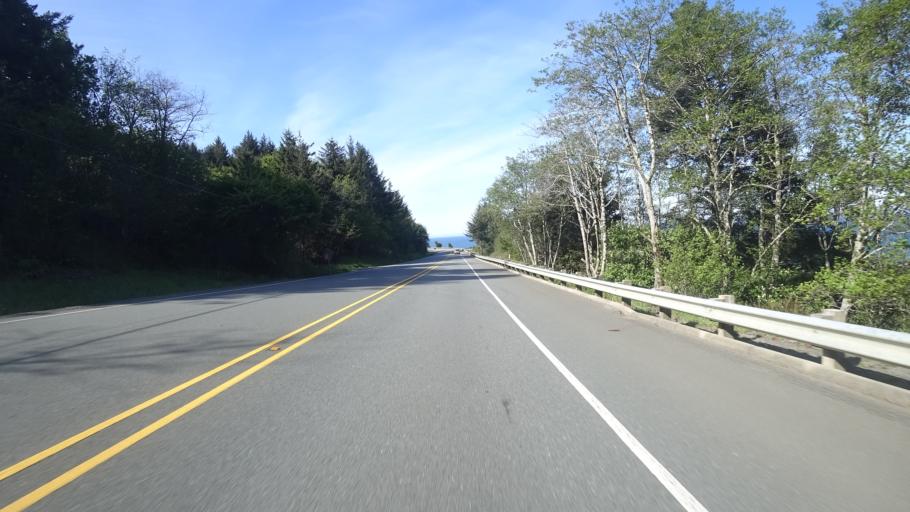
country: US
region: Oregon
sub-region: Curry County
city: Brookings
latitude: 42.2163
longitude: -124.3726
